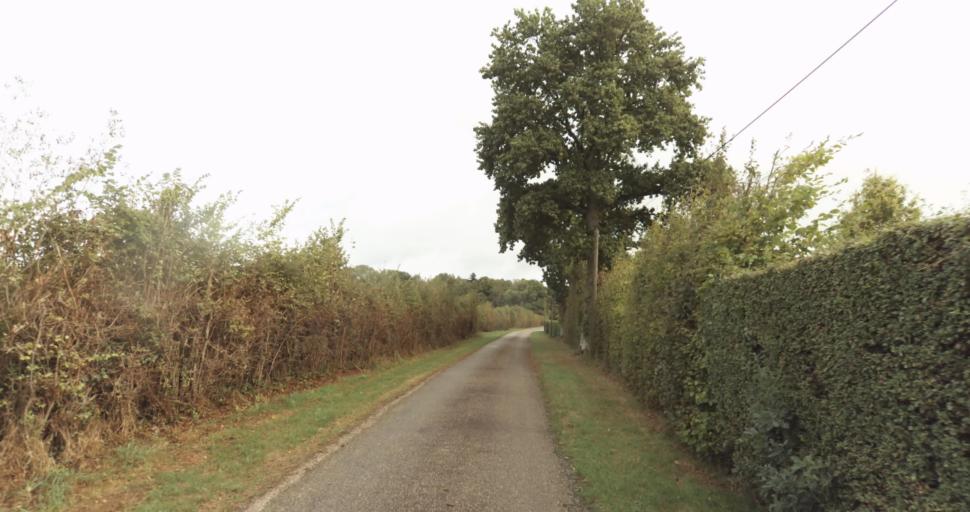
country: FR
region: Lower Normandy
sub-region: Departement de l'Orne
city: Gace
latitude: 48.8851
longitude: 0.3124
